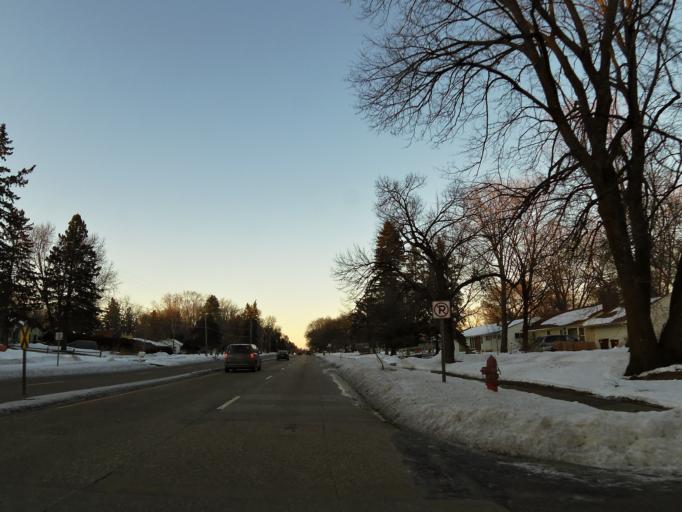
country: US
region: Minnesota
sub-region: Ramsey County
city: White Bear Lake
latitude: 45.0531
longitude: -93.0153
